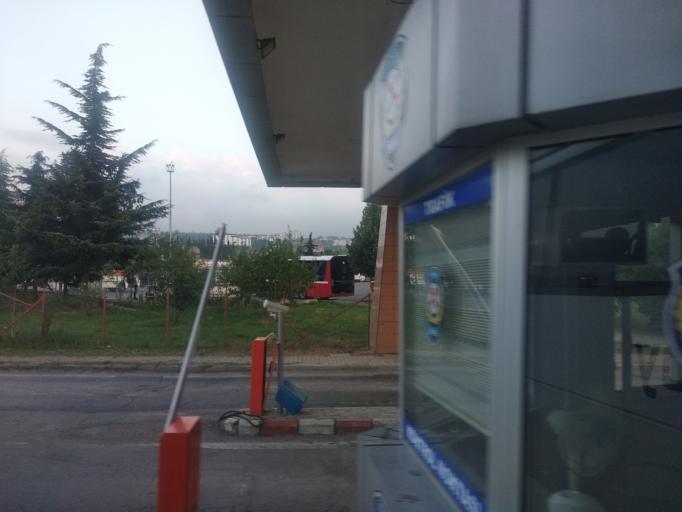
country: TR
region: Samsun
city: Samsun
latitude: 41.2882
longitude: 36.2882
